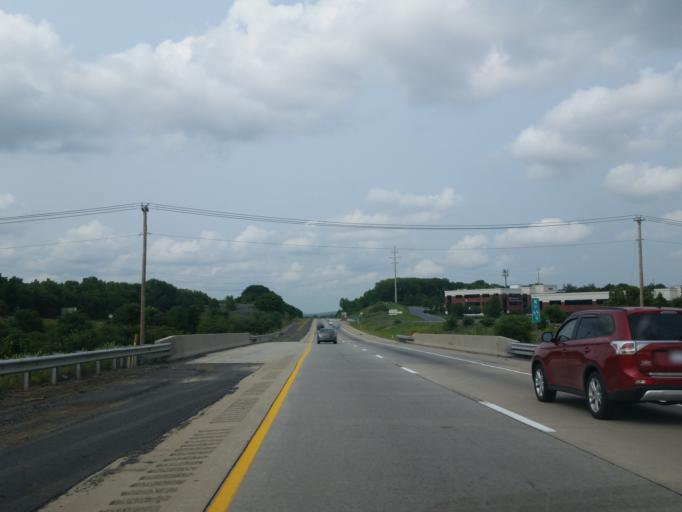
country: US
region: Pennsylvania
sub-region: Dauphin County
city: Colonial Park
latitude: 40.3107
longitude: -76.8321
